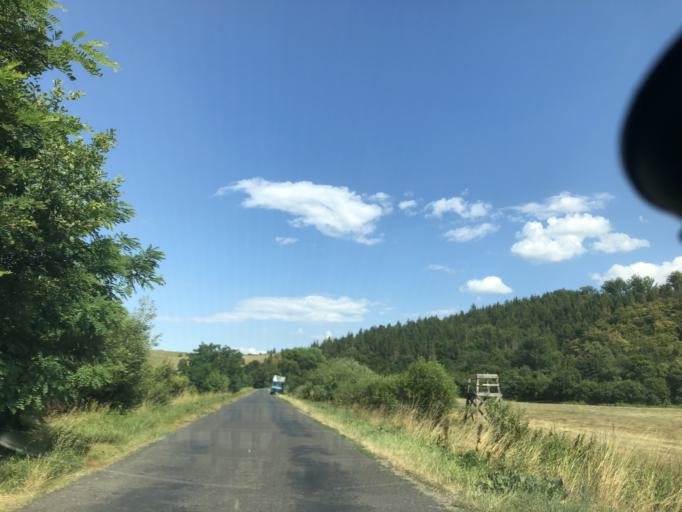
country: HU
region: Borsod-Abauj-Zemplen
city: Szendro
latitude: 48.5420
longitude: 20.7903
